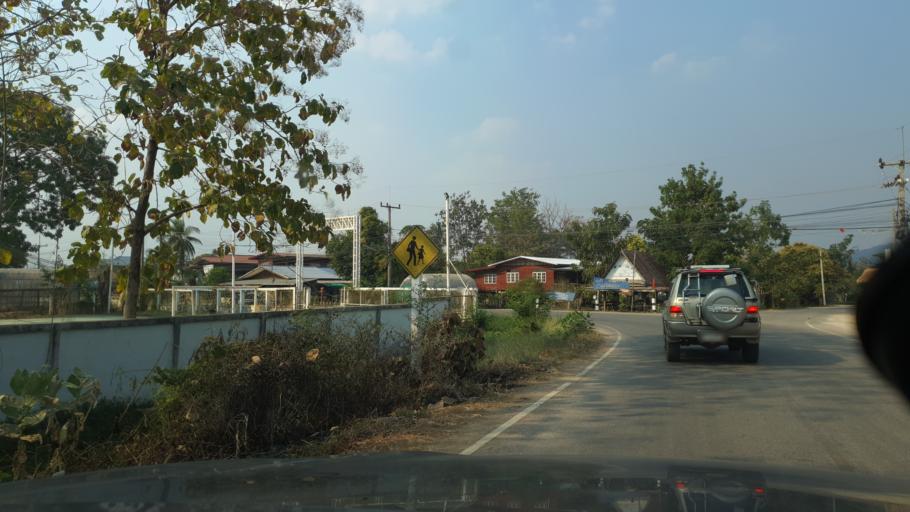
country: TH
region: Sukhothai
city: Ban Dan Lan Hoi
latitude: 17.1124
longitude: 99.5499
